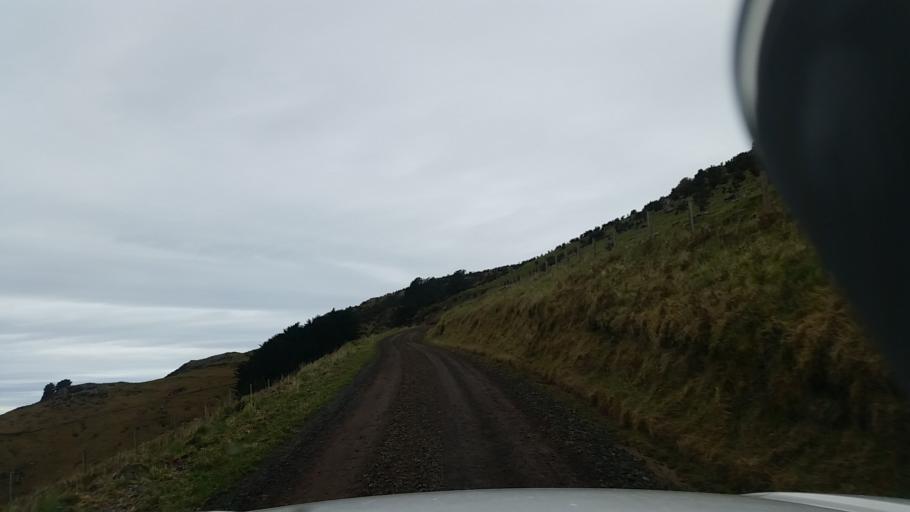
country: NZ
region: Canterbury
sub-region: Christchurch City
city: Christchurch
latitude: -43.7452
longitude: 173.0086
